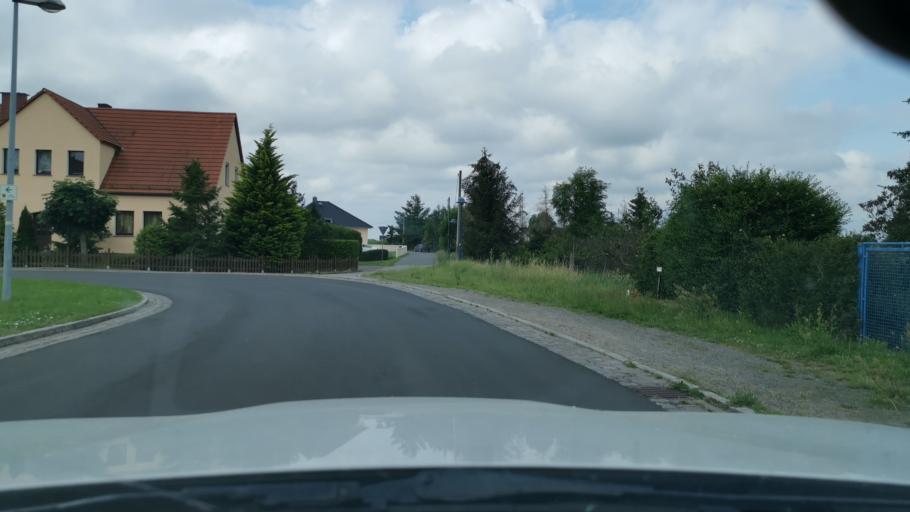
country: DE
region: Saxony
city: Torgau
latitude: 51.6057
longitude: 13.0253
